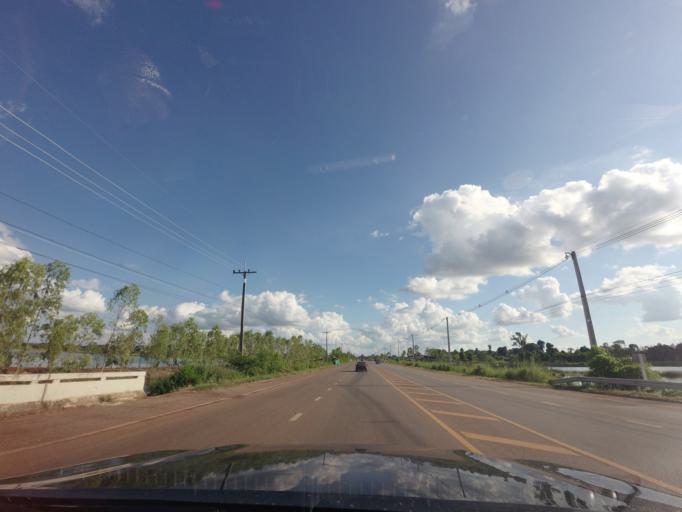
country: TH
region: Changwat Udon Thani
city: Ban Dung
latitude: 17.7194
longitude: 103.2502
